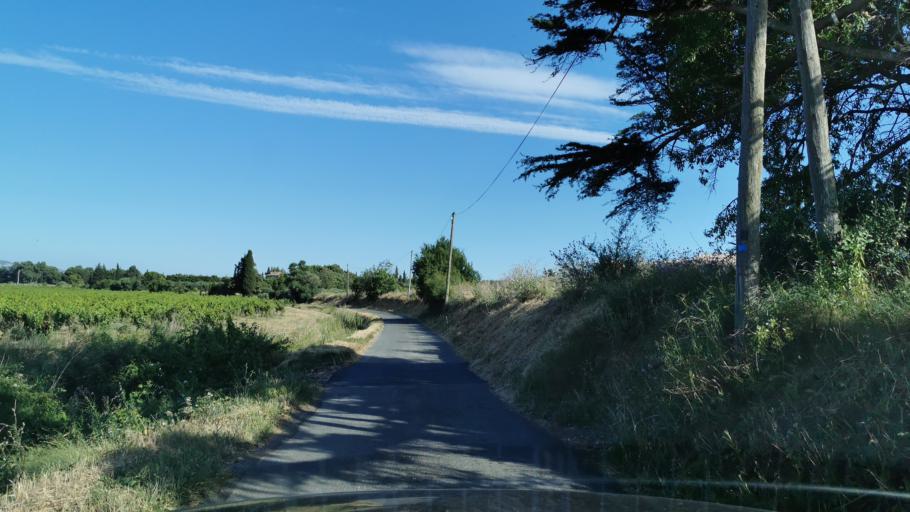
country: FR
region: Languedoc-Roussillon
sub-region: Departement de l'Aude
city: Narbonne
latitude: 43.1610
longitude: 2.9996
